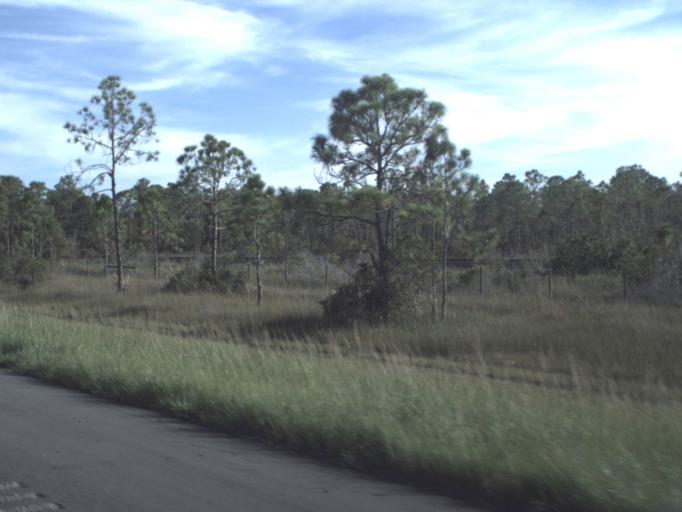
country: US
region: Florida
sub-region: Lee County
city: Burnt Store Marina
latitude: 26.8317
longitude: -81.9562
